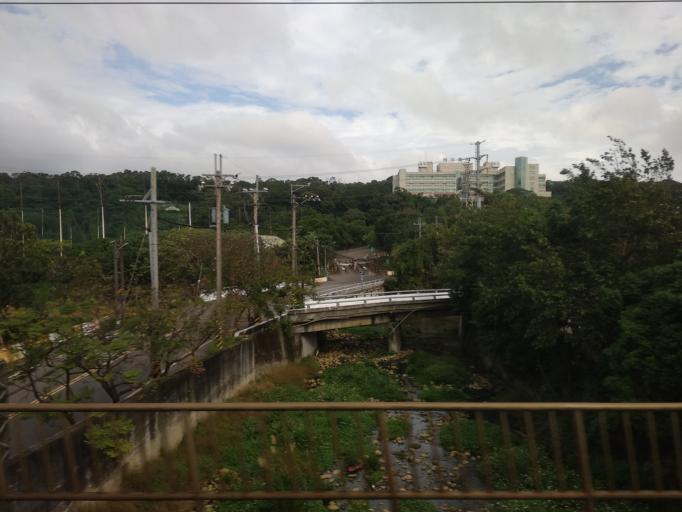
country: TW
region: Taiwan
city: Daxi
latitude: 24.9139
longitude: 121.1545
